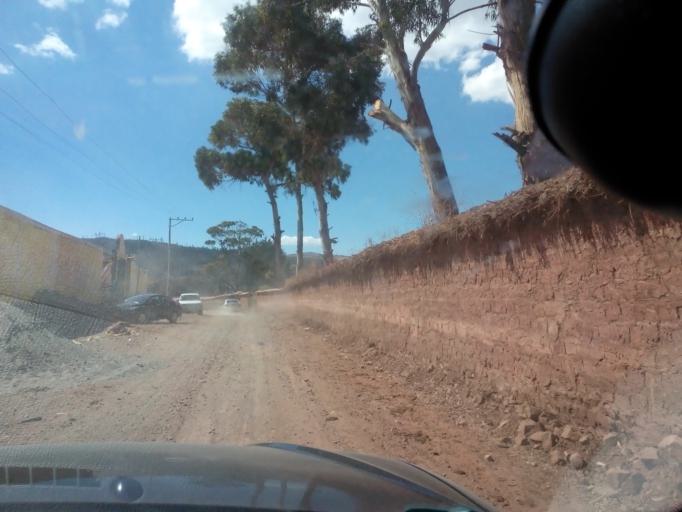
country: PE
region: Cusco
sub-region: Provincia de Anta
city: Huarocondo
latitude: -13.4191
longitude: -72.2101
